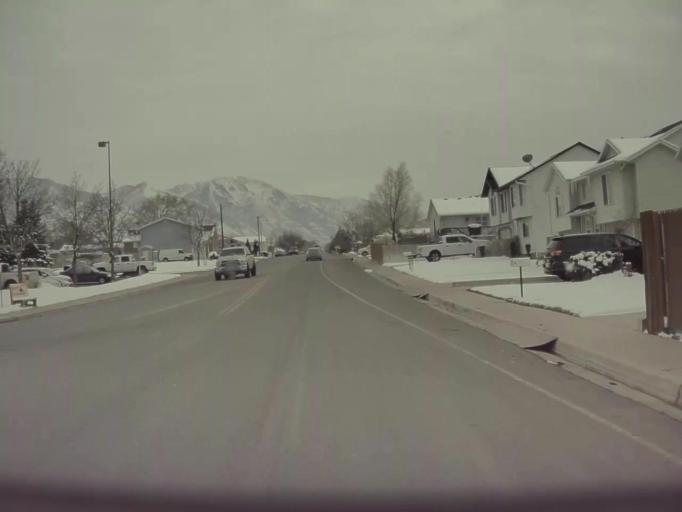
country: US
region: Utah
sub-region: Utah County
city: Spanish Fork
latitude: 40.1183
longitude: -111.6407
